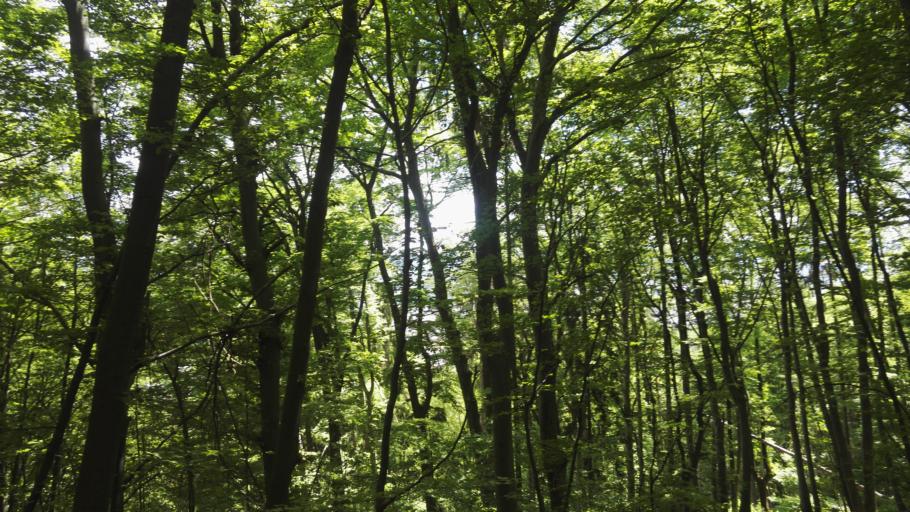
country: AT
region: Styria
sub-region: Graz Stadt
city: Goesting
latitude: 47.0881
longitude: 15.3895
